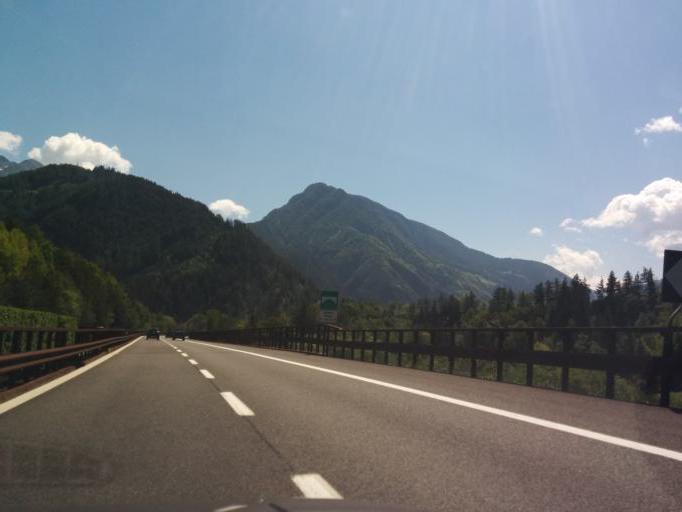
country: IT
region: Trentino-Alto Adige
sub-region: Bolzano
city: Campo di Trens
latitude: 46.8621
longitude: 11.5007
